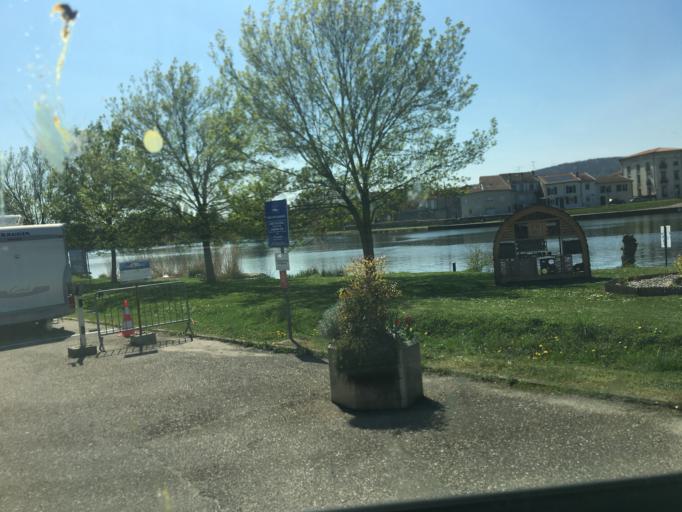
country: FR
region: Lorraine
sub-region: Departement de Meurthe-et-Moselle
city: Pont-a-Mousson
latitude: 48.9029
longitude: 6.0610
